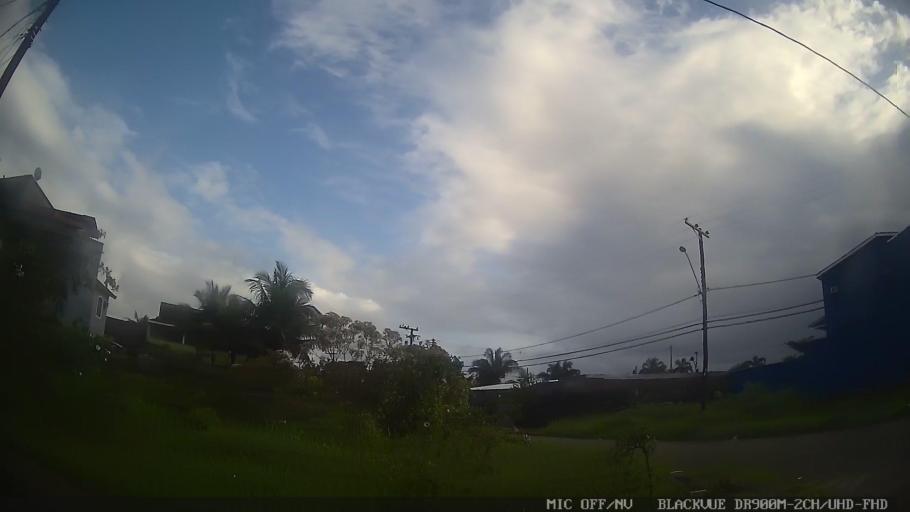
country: BR
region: Sao Paulo
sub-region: Itanhaem
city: Itanhaem
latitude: -24.2357
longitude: -46.8844
